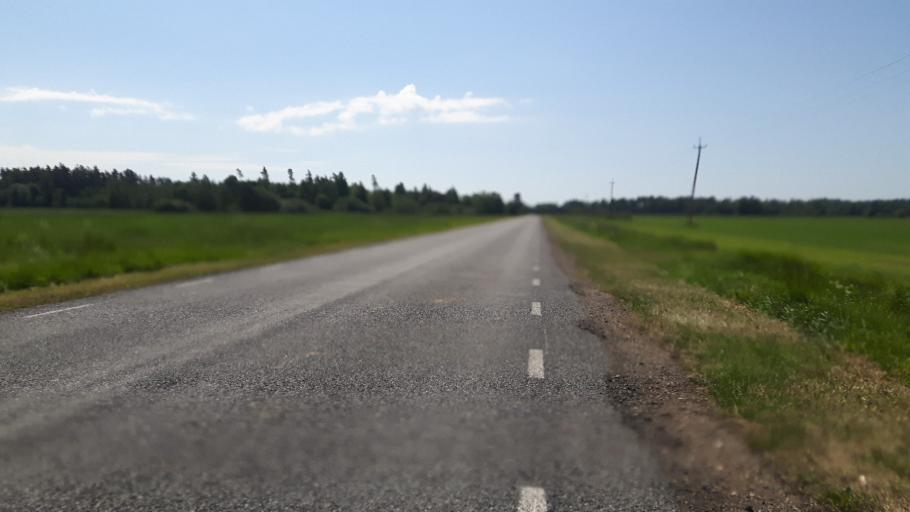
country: EE
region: Paernumaa
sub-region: Vaendra vald (alev)
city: Vandra
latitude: 58.6094
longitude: 25.0214
